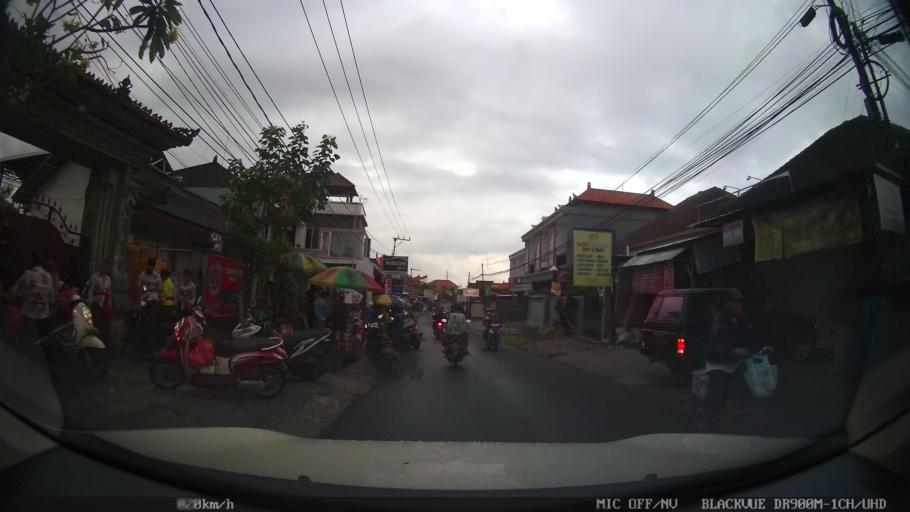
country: ID
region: Bali
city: Banjar Kertajiwa
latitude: -8.6265
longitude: 115.2664
